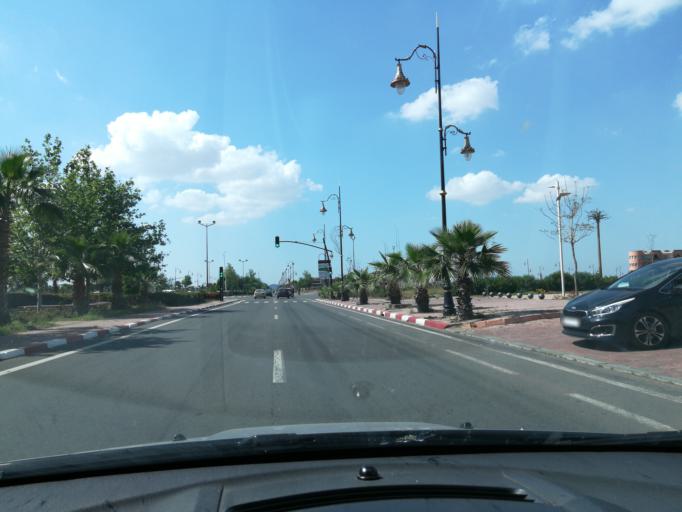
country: MA
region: Marrakech-Tensift-Al Haouz
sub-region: Marrakech
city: Marrakesh
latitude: 31.5942
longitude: -7.9924
